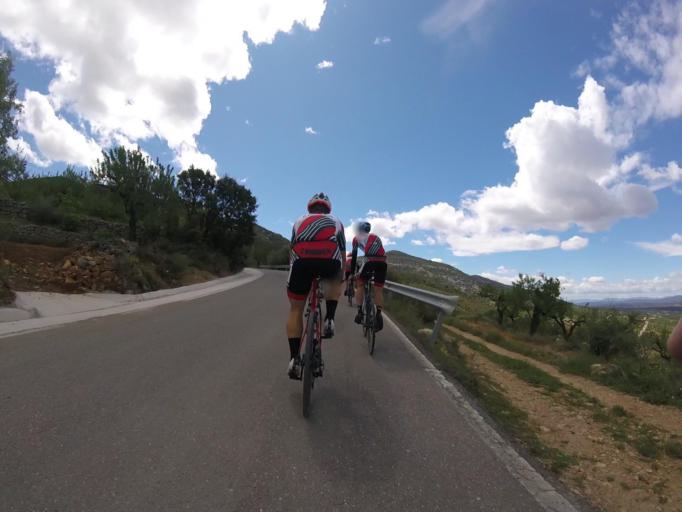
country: ES
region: Valencia
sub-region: Provincia de Castello
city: Sierra-Engarceran
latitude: 40.2939
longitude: -0.0415
